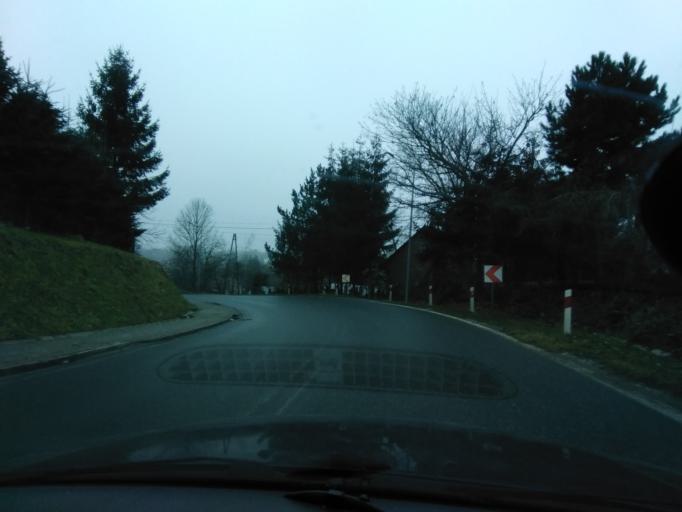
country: PL
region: Subcarpathian Voivodeship
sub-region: Powiat lancucki
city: Sonina
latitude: 50.0571
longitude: 22.2761
